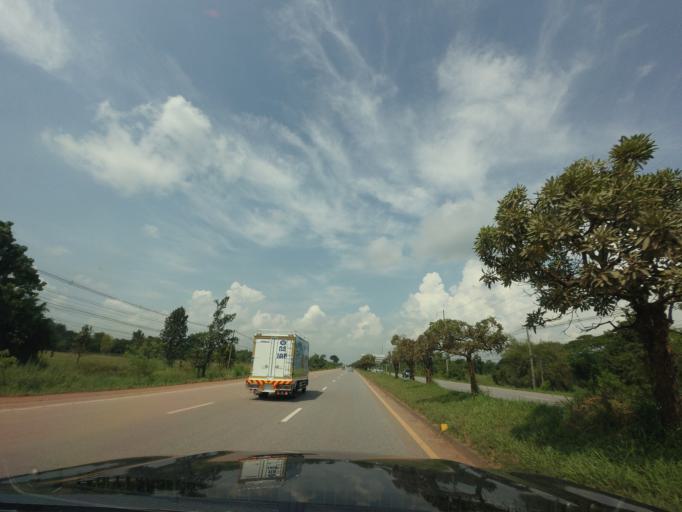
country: TH
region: Khon Kaen
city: Khon Kaen
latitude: 16.4505
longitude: 102.7364
